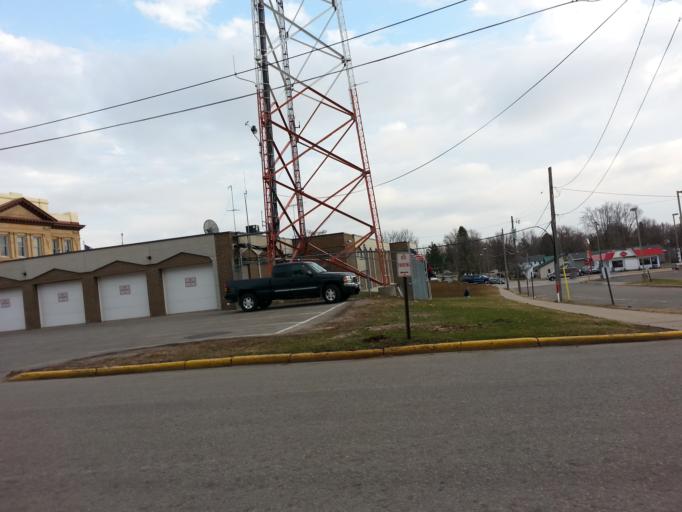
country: US
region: Wisconsin
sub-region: Pierce County
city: Ellsworth
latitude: 44.7330
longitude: -92.4857
